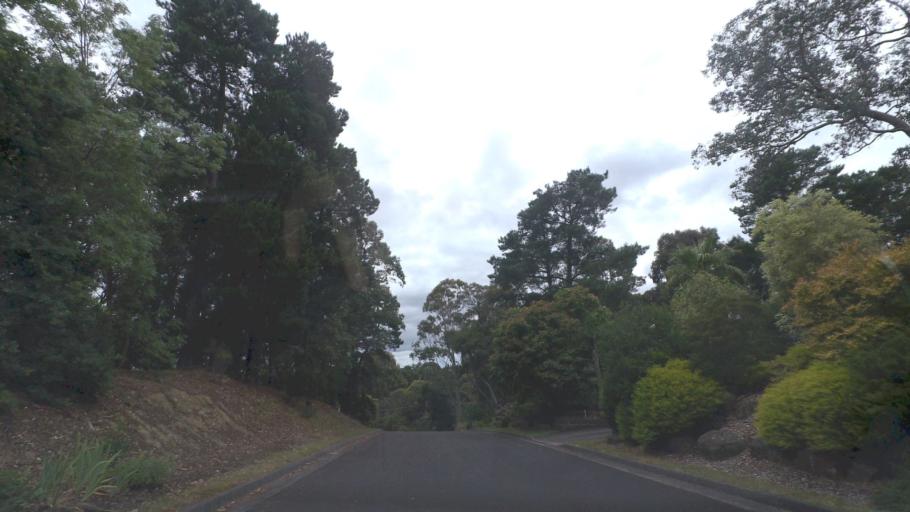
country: AU
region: Victoria
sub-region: Manningham
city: Park Orchards
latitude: -37.7882
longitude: 145.2063
